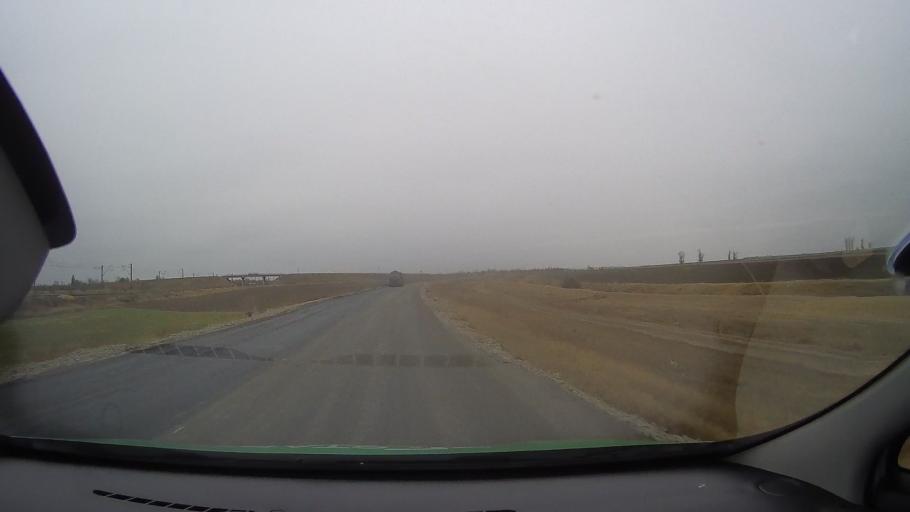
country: RO
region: Braila
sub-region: Comuna Baraganul
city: Baraganul
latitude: 44.8039
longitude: 27.5250
